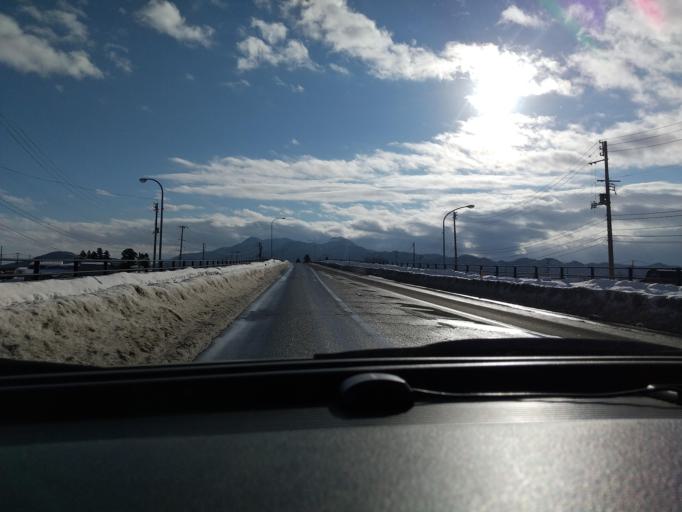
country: JP
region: Iwate
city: Morioka-shi
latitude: 39.7173
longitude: 141.0840
